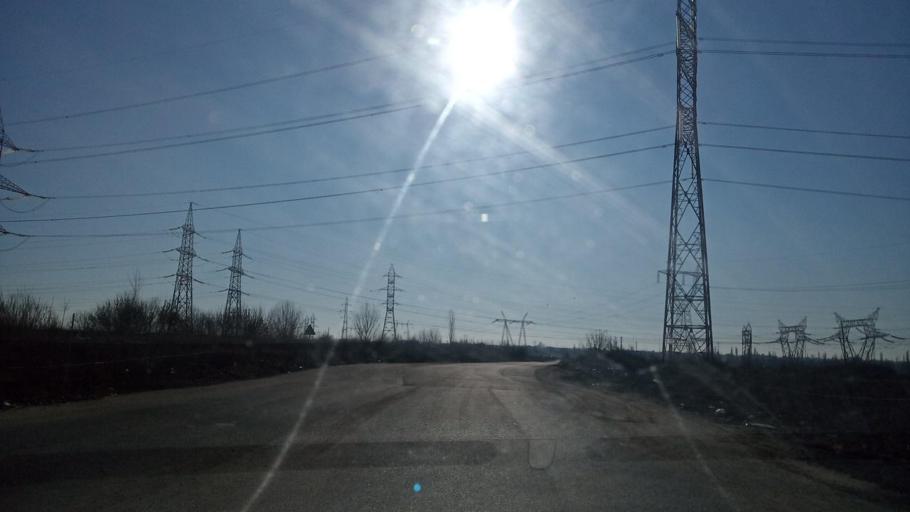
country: RO
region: Ilfov
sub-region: Comuna Popesti-Leordeni
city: Popesti-Leordeni
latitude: 44.3975
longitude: 26.1834
